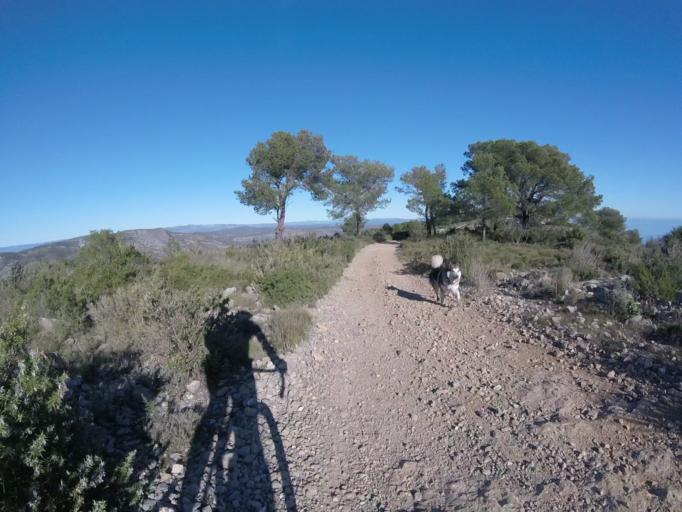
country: ES
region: Valencia
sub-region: Provincia de Castello
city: Orpesa/Oropesa del Mar
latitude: 40.0987
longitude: 0.1103
